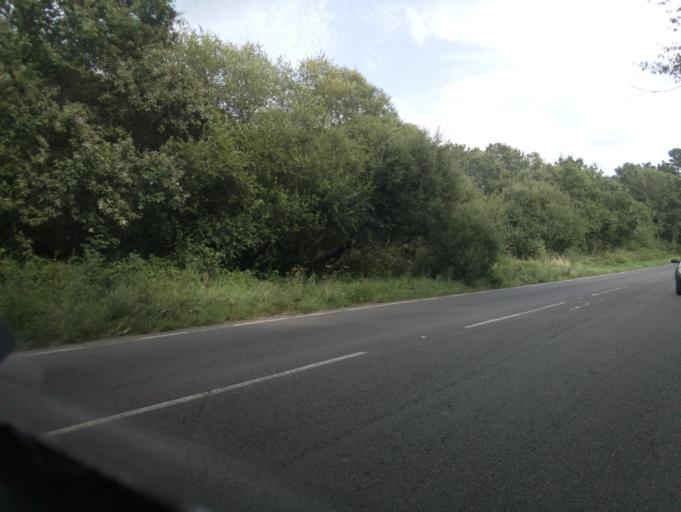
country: GB
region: England
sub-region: Hampshire
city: Hythe
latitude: 50.8627
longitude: -1.4338
